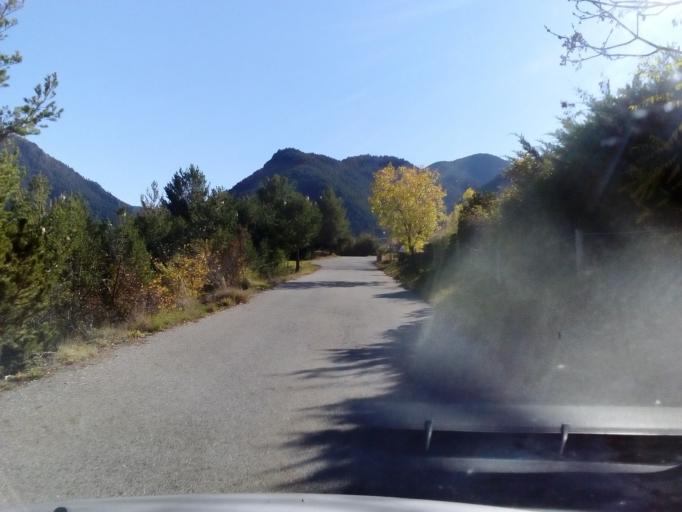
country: ES
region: Catalonia
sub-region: Provincia de Lleida
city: Bellver de Cerdanya
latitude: 42.3449
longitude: 1.7773
